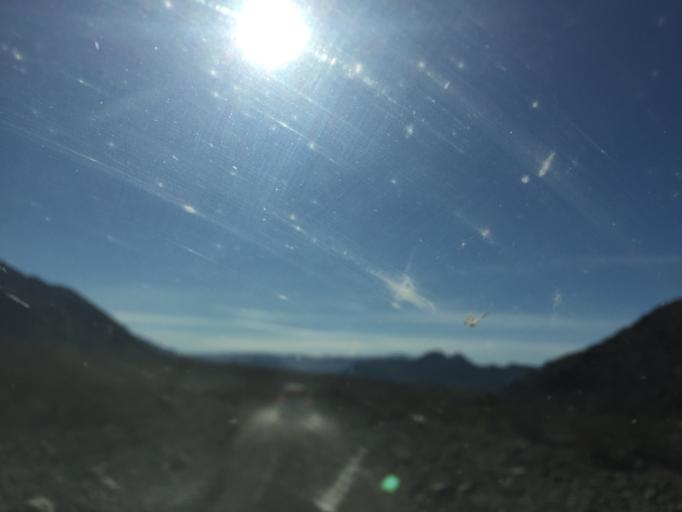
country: US
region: California
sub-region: Inyo County
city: Lone Pine
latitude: 36.7637
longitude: -117.5375
